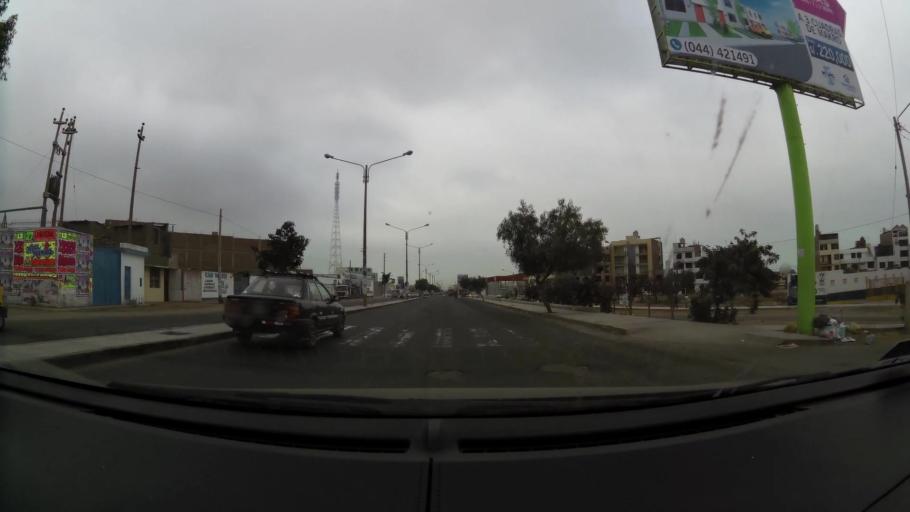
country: PE
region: La Libertad
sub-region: Provincia de Trujillo
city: La Esperanza
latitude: -8.0856
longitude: -79.0433
